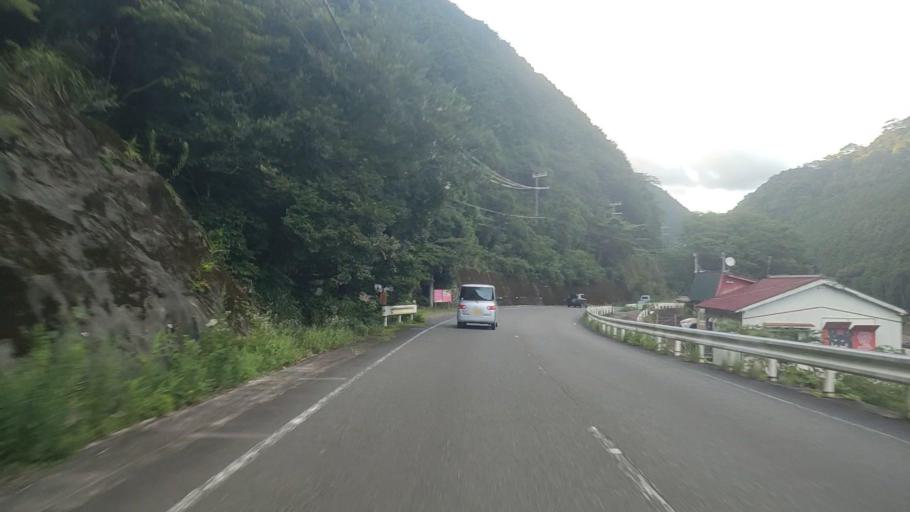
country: JP
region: Wakayama
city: Tanabe
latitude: 33.7671
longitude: 135.4997
